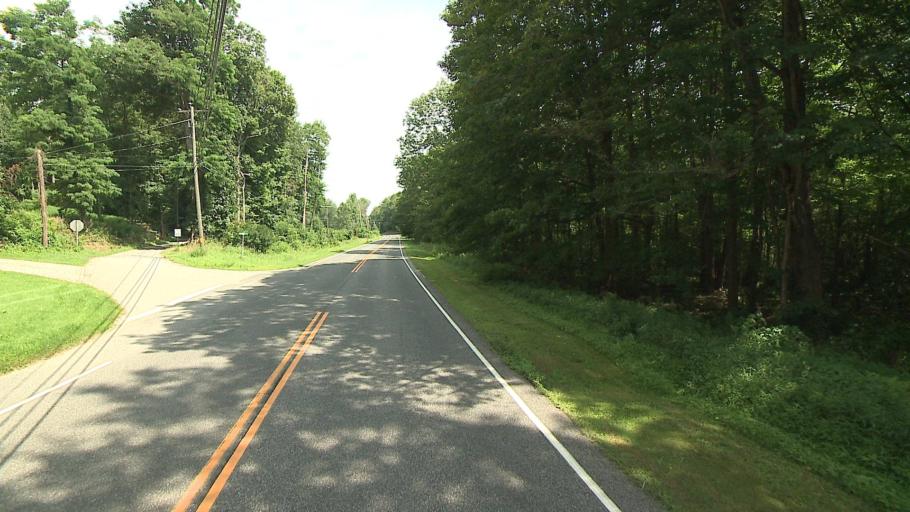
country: US
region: Connecticut
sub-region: Fairfield County
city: Sherman
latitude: 41.5884
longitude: -73.4986
